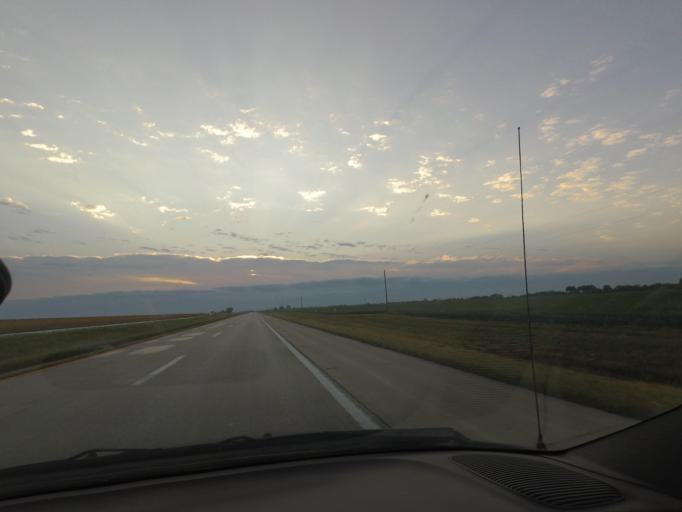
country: US
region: Missouri
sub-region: Macon County
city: Macon
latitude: 39.7498
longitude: -92.3073
